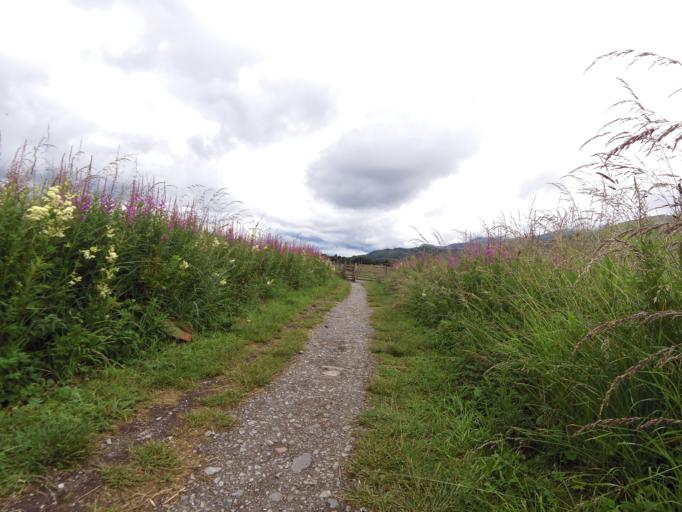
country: GB
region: Scotland
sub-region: Highland
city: Fort William
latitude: 56.8299
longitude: -5.0912
